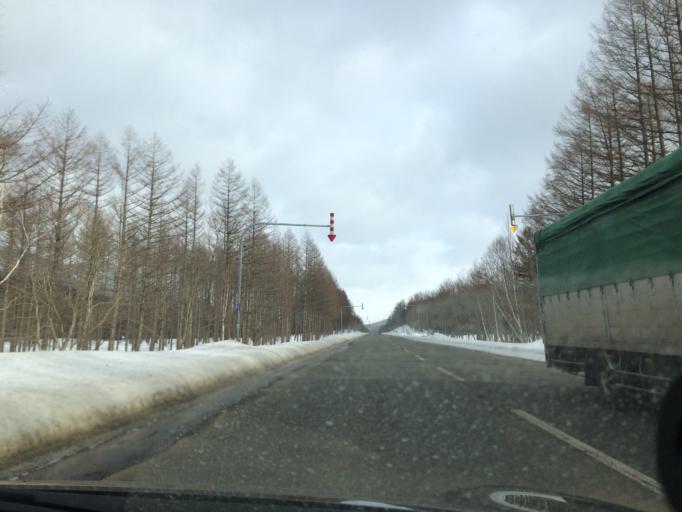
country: JP
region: Hokkaido
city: Shimo-furano
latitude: 43.1314
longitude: 142.6966
